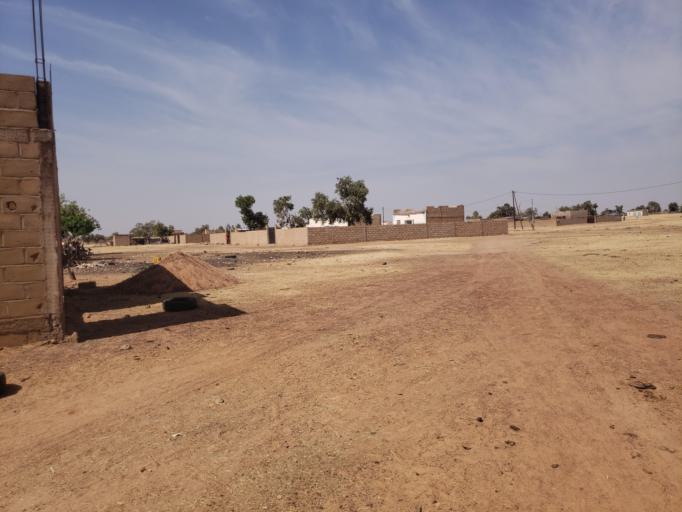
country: SN
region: Matam
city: Ranerou
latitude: 15.2997
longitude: -13.9641
